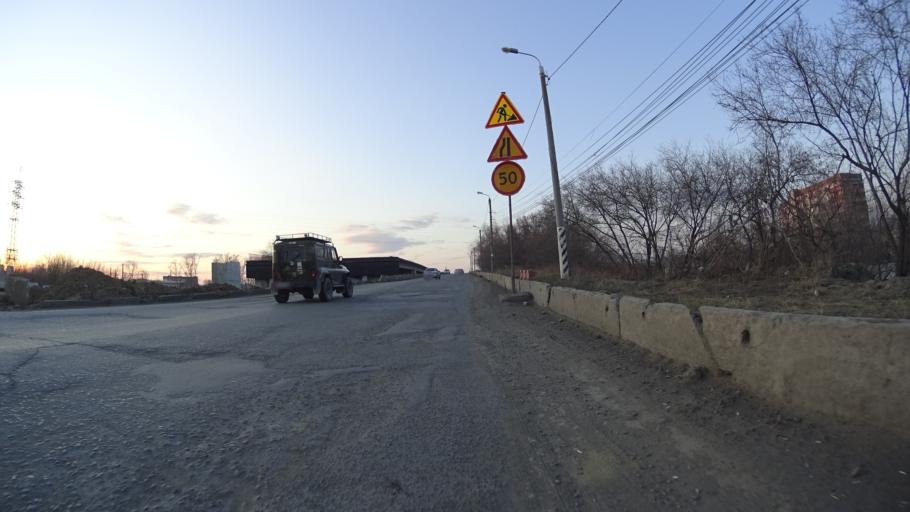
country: RU
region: Chelyabinsk
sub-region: Gorod Chelyabinsk
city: Chelyabinsk
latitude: 55.1141
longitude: 61.3864
